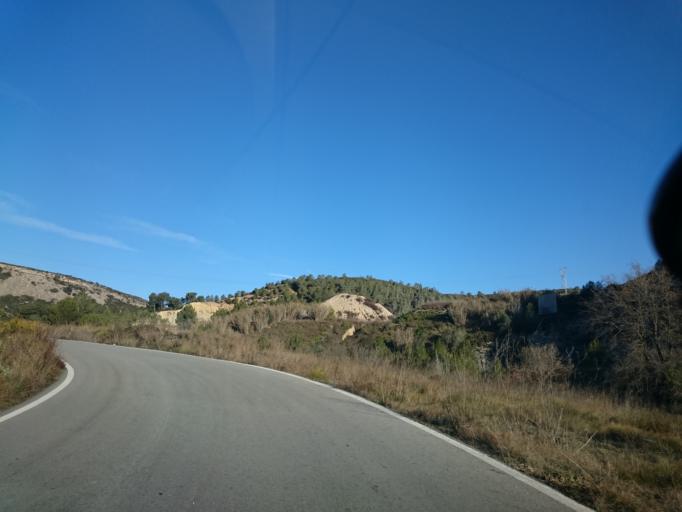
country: ES
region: Catalonia
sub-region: Provincia de Barcelona
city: Vilafranca del Penedes
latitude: 41.3082
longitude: 1.7255
